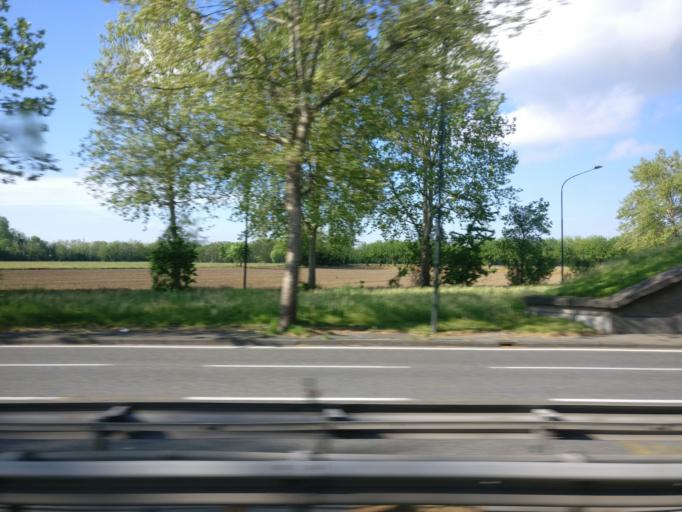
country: IT
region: Piedmont
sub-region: Provincia di Torino
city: Savonera
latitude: 45.0997
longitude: 7.6172
